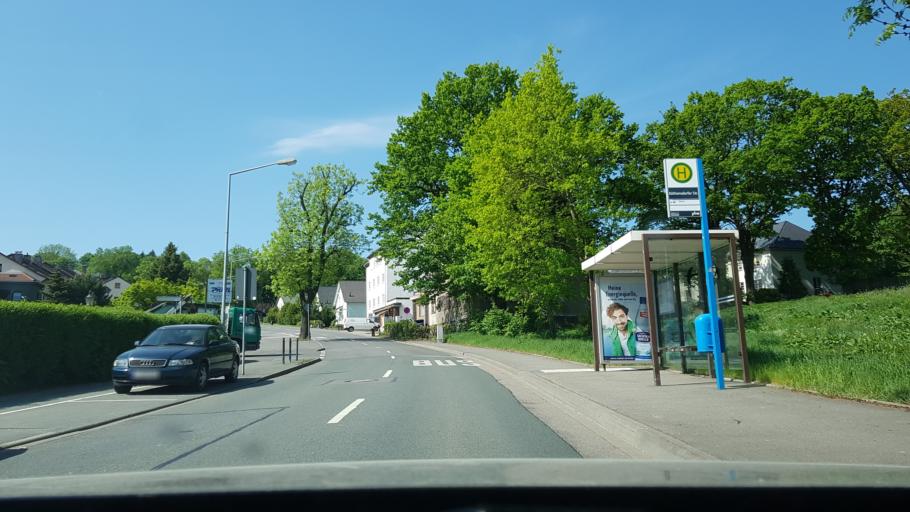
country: DE
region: Saxony
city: Wittgensdorf
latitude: 50.8572
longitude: 12.8853
